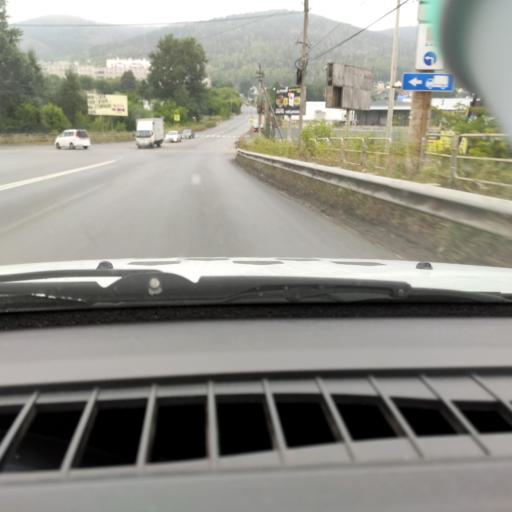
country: RU
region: Chelyabinsk
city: Miass
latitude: 55.0300
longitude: 60.1178
